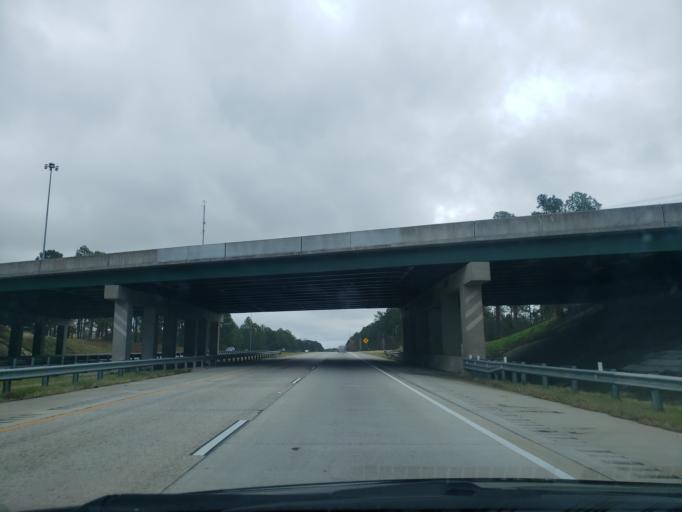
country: US
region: Georgia
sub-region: Laurens County
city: Dublin
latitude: 32.4876
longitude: -82.9355
